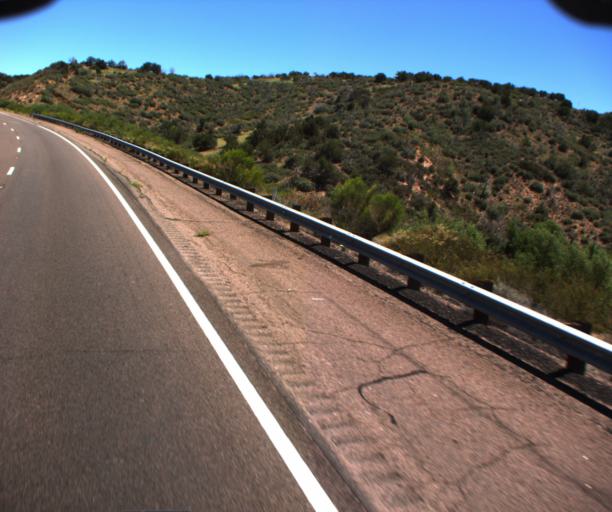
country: US
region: Arizona
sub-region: Gila County
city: Tonto Basin
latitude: 34.0108
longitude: -111.3593
